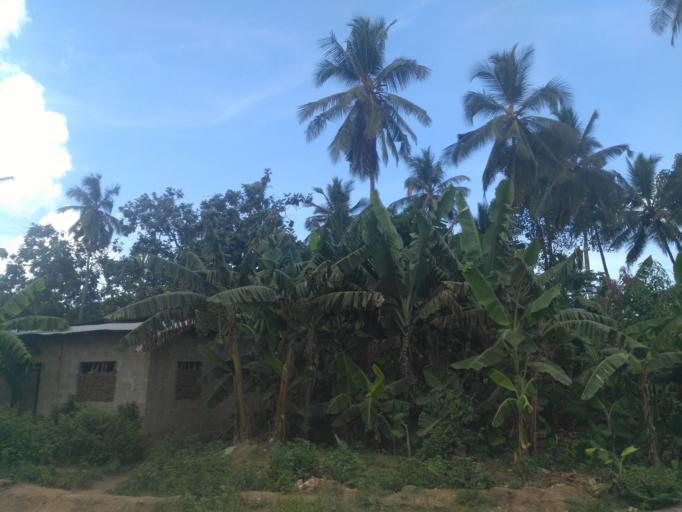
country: TZ
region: Zanzibar North
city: Gamba
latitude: -5.9740
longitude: 39.2993
